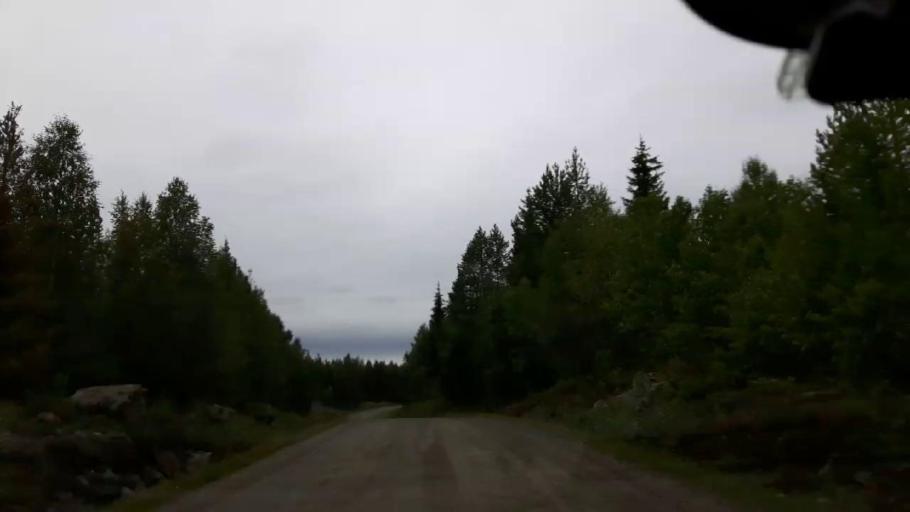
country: SE
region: Vaesternorrland
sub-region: Ange Kommun
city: Fransta
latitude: 62.8581
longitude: 15.9818
